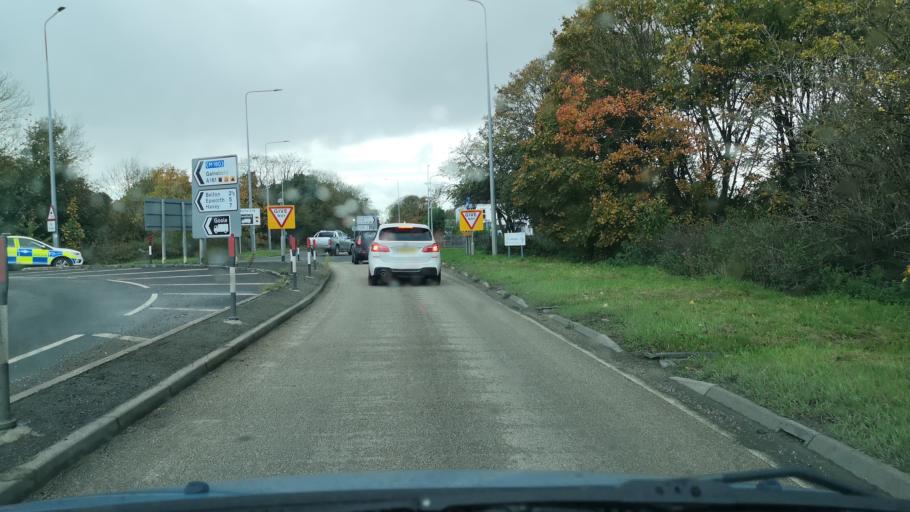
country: GB
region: England
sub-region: North Lincolnshire
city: Crowle
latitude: 53.5856
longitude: -0.8185
